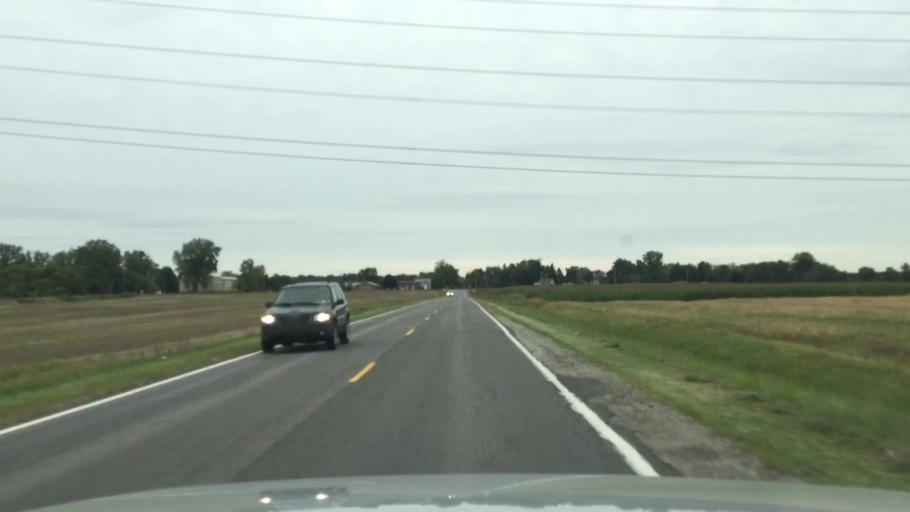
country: US
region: Michigan
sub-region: Washtenaw County
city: Milan
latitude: 42.1193
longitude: -83.6961
